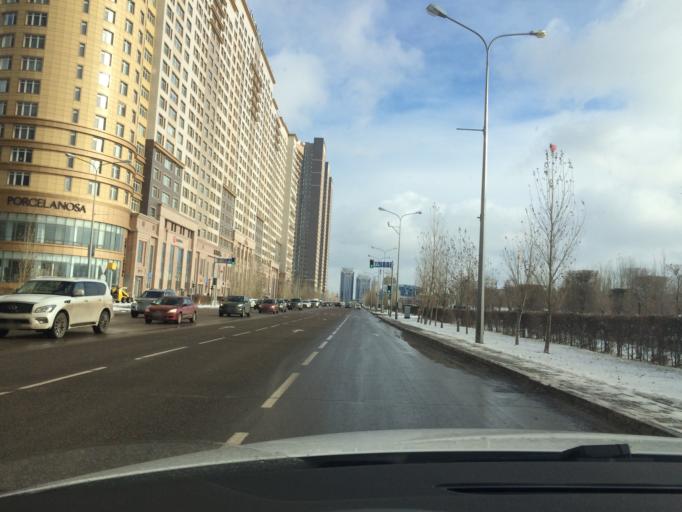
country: KZ
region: Astana Qalasy
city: Astana
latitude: 51.1272
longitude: 71.4595
